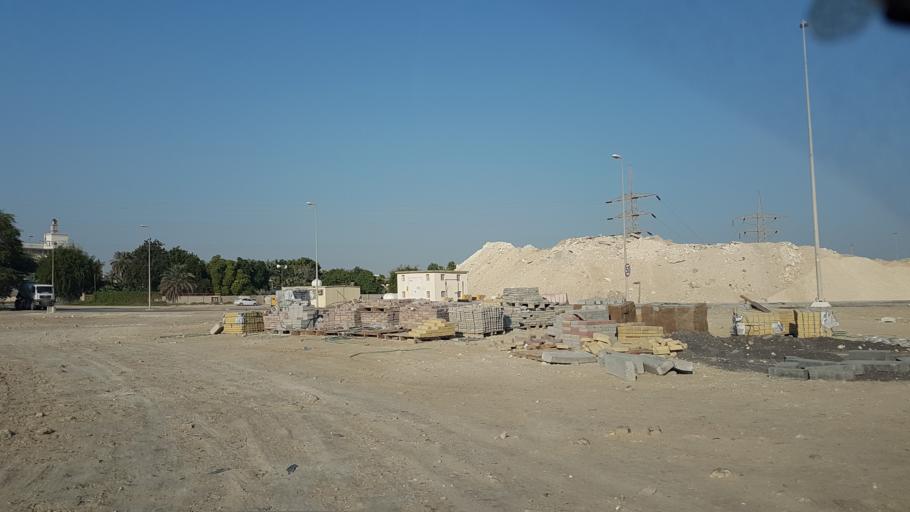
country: BH
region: Northern
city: Ar Rifa'
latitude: 26.1255
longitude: 50.5929
